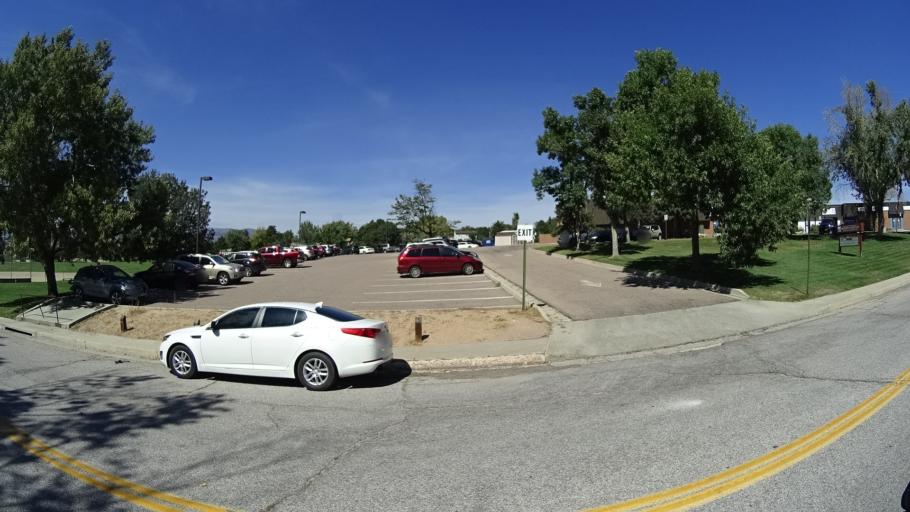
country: US
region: Colorado
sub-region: El Paso County
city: Cimarron Hills
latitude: 38.9060
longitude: -104.7709
